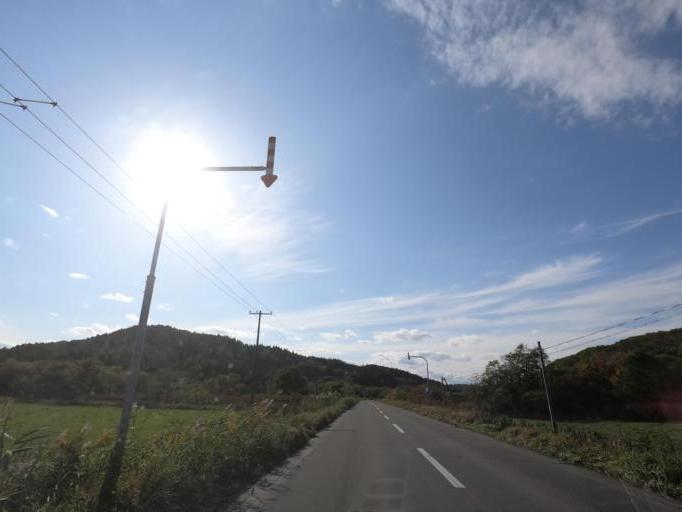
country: JP
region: Hokkaido
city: Obihiro
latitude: 42.6178
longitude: 143.4187
